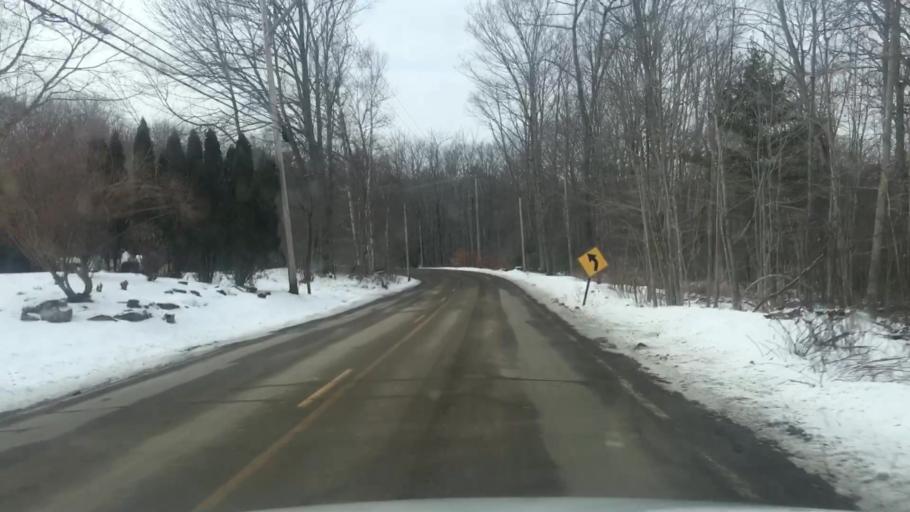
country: US
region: Maine
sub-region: Waldo County
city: Lincolnville
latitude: 44.2912
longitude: -69.0718
